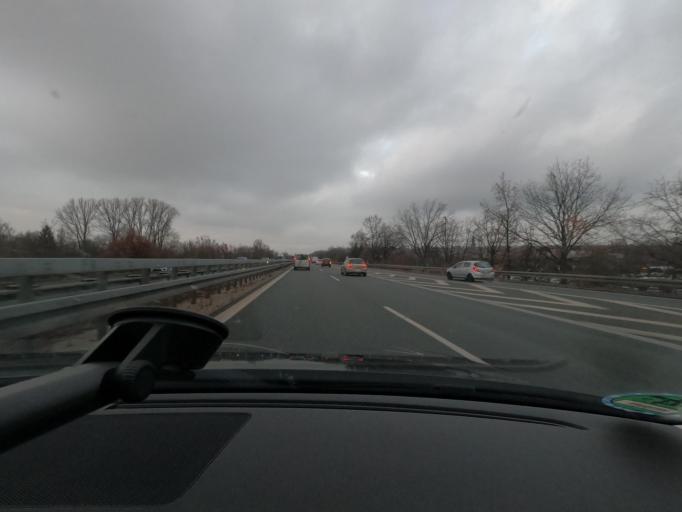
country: DE
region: Bavaria
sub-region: Regierungsbezirk Mittelfranken
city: Erlangen
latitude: 49.5961
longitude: 10.9982
